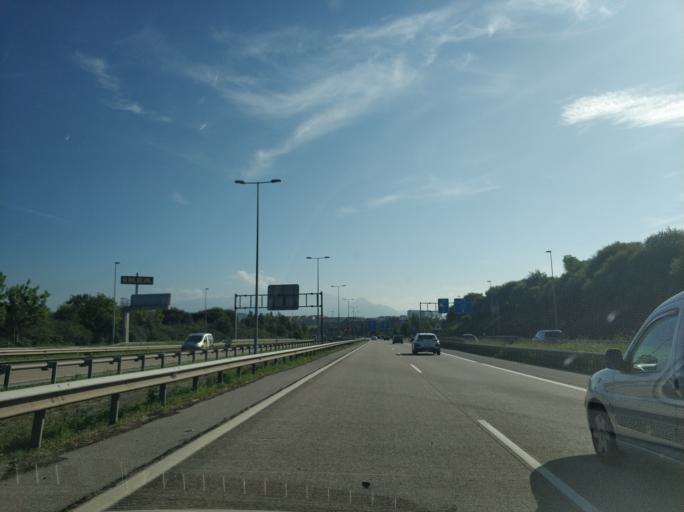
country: ES
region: Asturias
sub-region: Province of Asturias
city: Lugones
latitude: 43.3907
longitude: -5.8064
